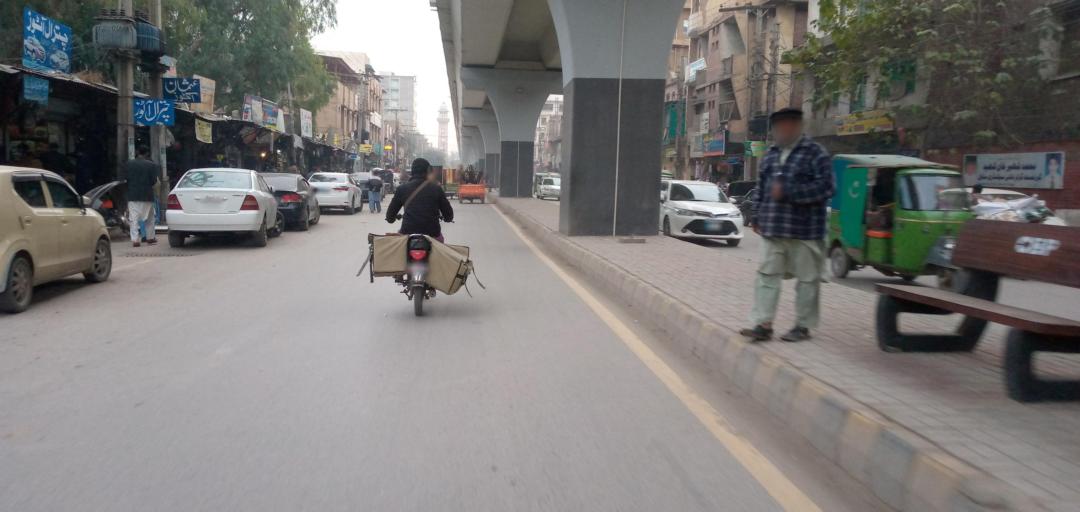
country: PK
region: Khyber Pakhtunkhwa
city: Peshawar
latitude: 33.9982
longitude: 71.5432
